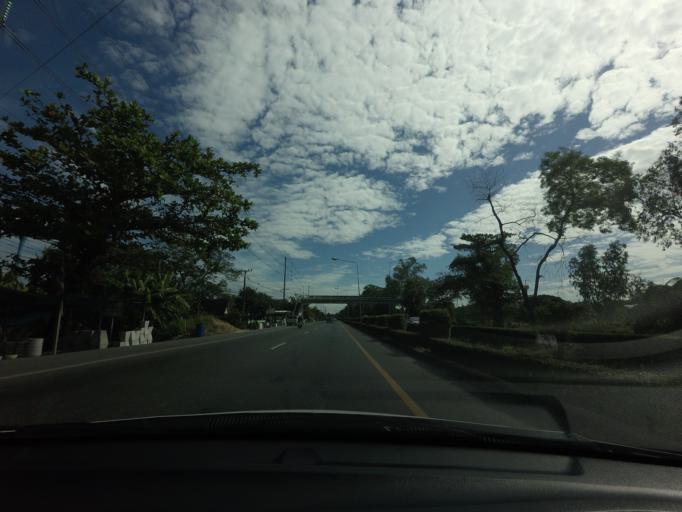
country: TH
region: Nakhon Nayok
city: Ongkharak
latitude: 14.0879
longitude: 100.9250
